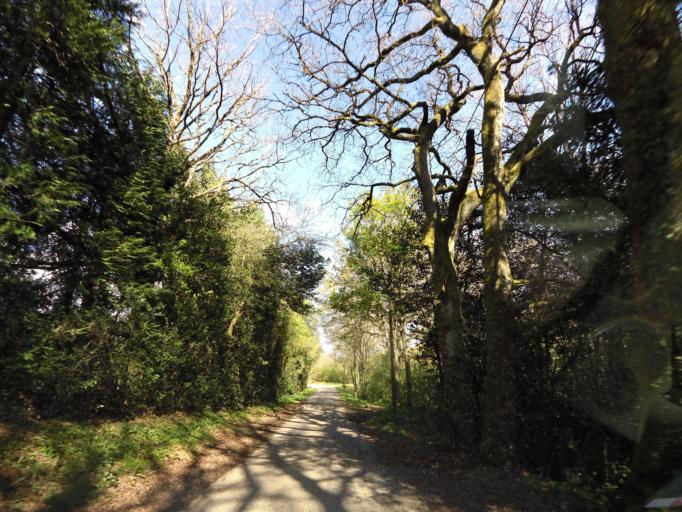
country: FR
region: Midi-Pyrenees
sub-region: Departement du Tarn
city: Soreze
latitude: 43.3941
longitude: 2.0907
